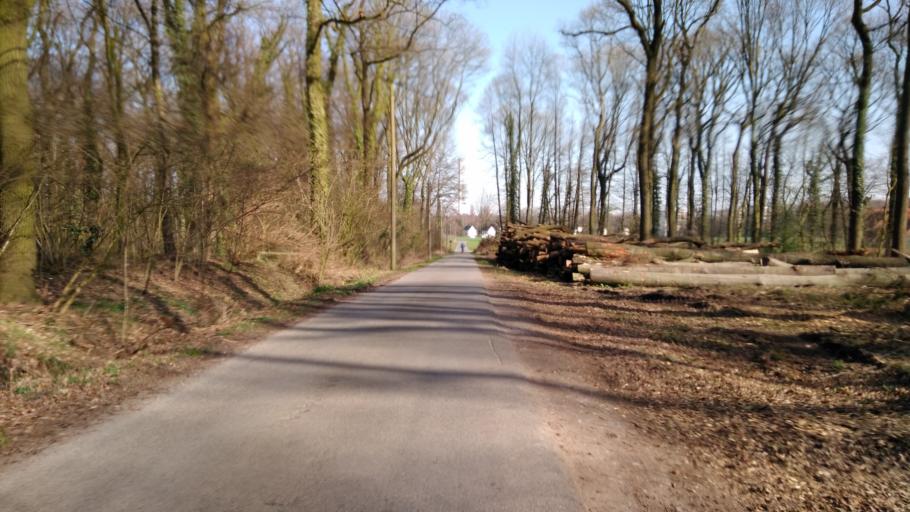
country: DE
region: North Rhine-Westphalia
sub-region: Regierungsbezirk Munster
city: Gladbeck
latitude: 51.5968
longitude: 6.9554
